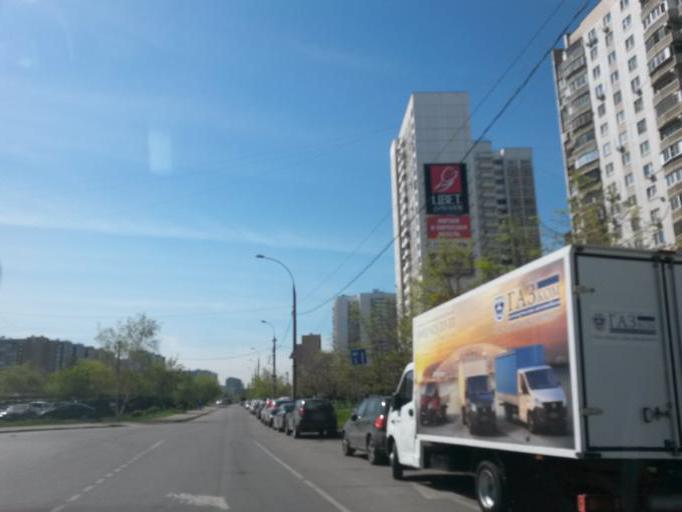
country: RU
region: Moscow
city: Mar'ino
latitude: 55.6480
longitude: 37.7403
